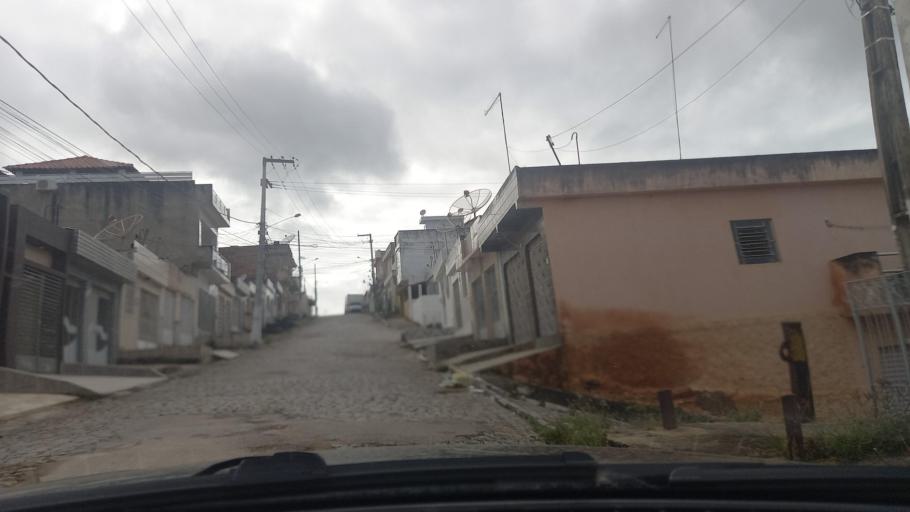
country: BR
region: Pernambuco
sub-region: Vitoria De Santo Antao
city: Vitoria de Santo Antao
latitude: -8.1113
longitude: -35.3003
